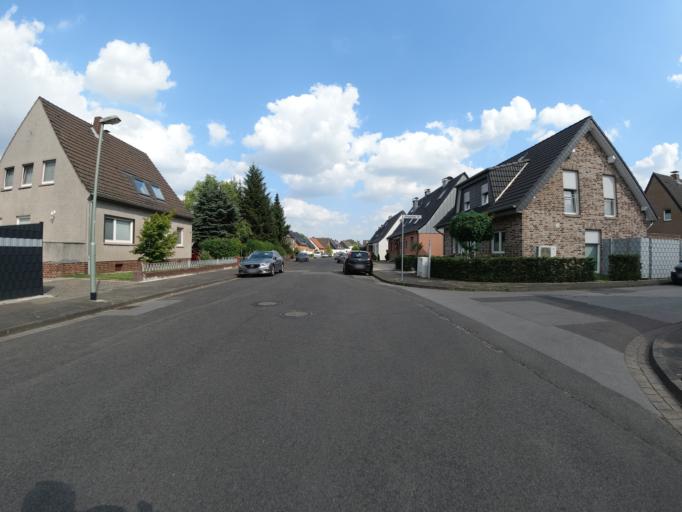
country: DE
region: North Rhine-Westphalia
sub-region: Regierungsbezirk Dusseldorf
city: Moers
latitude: 51.3964
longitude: 6.6792
